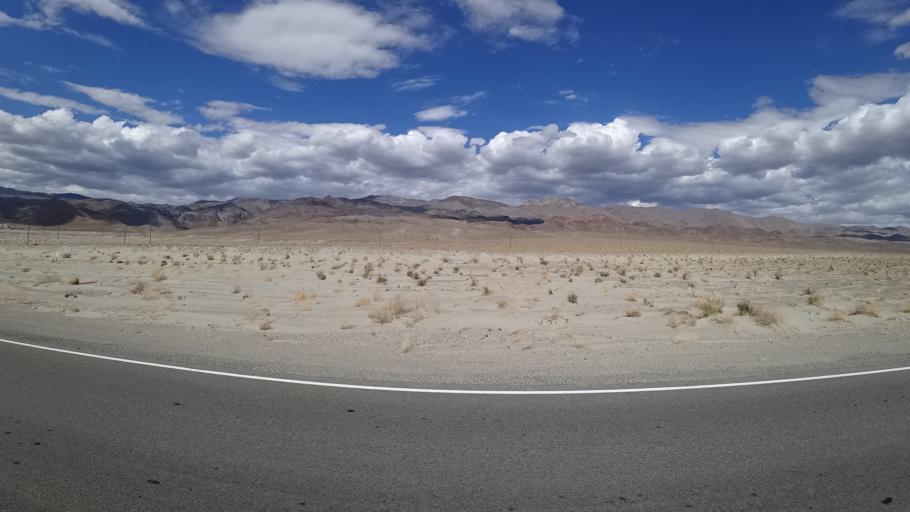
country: US
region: California
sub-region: Inyo County
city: Lone Pine
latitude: 36.4951
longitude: -117.8771
